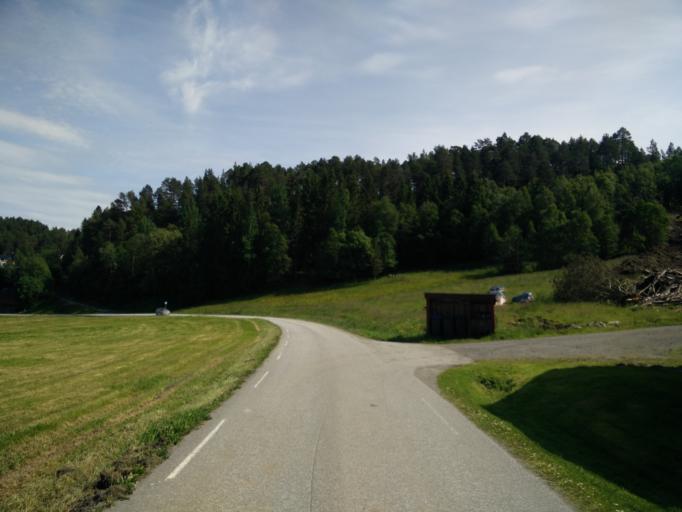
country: NO
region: More og Romsdal
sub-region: Kristiansund
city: Rensvik
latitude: 63.0189
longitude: 7.9494
